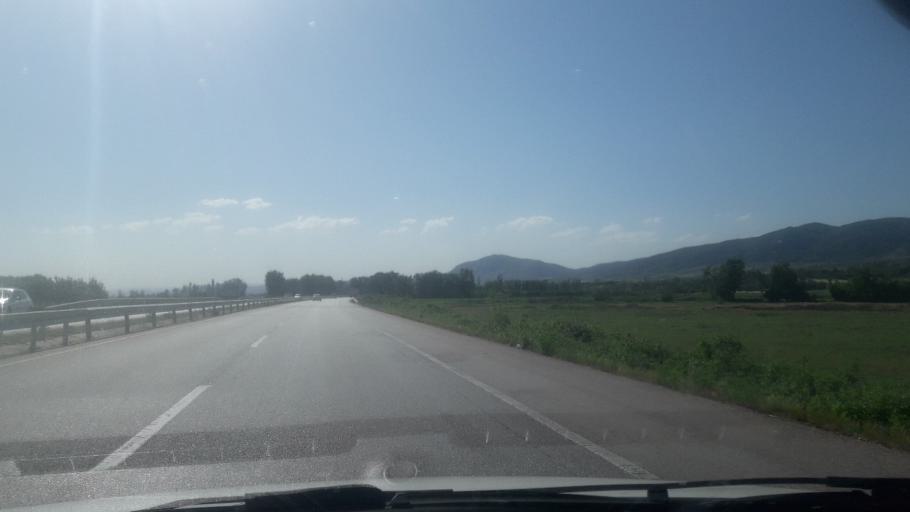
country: TR
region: Tokat
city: Dokmetepe
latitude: 40.3046
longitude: 36.3122
